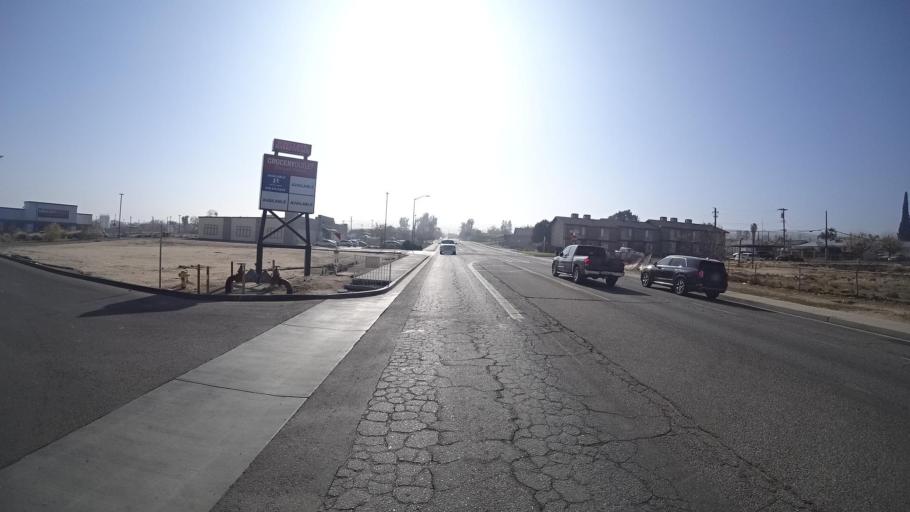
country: US
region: California
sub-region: Kern County
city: Taft
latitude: 35.1405
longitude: -119.4651
